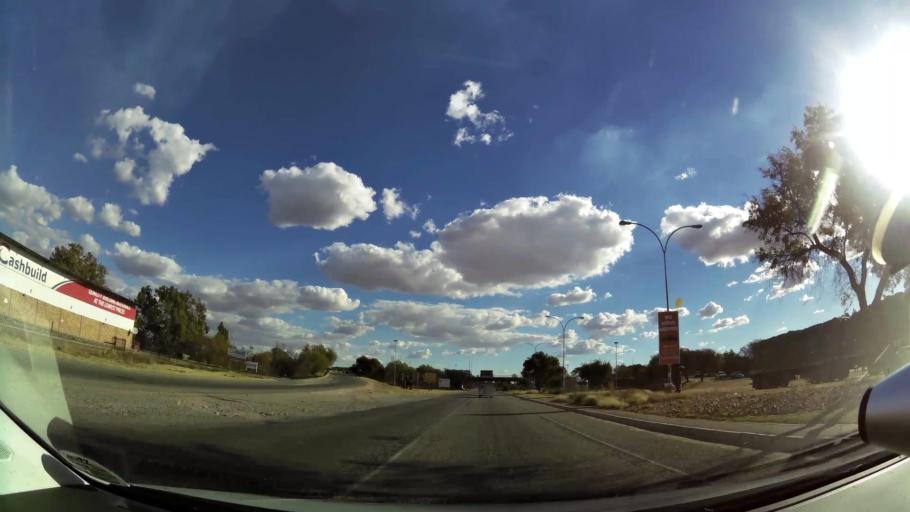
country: ZA
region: North-West
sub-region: Dr Kenneth Kaunda District Municipality
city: Klerksdorp
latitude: -26.8601
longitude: 26.6675
